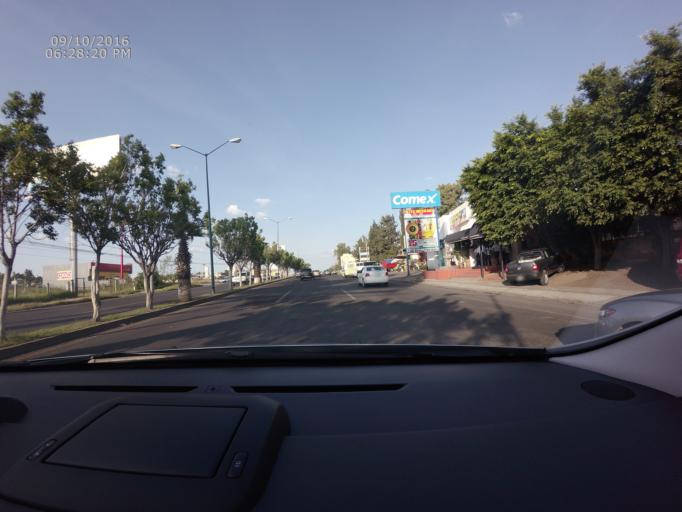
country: MX
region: Michoacan
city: Morelia
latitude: 19.6728
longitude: -101.2071
